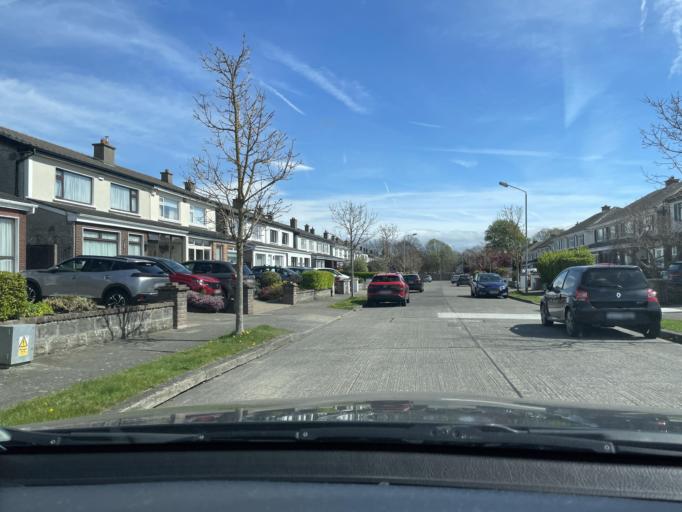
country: IE
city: Killester
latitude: 53.3689
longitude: -6.1971
